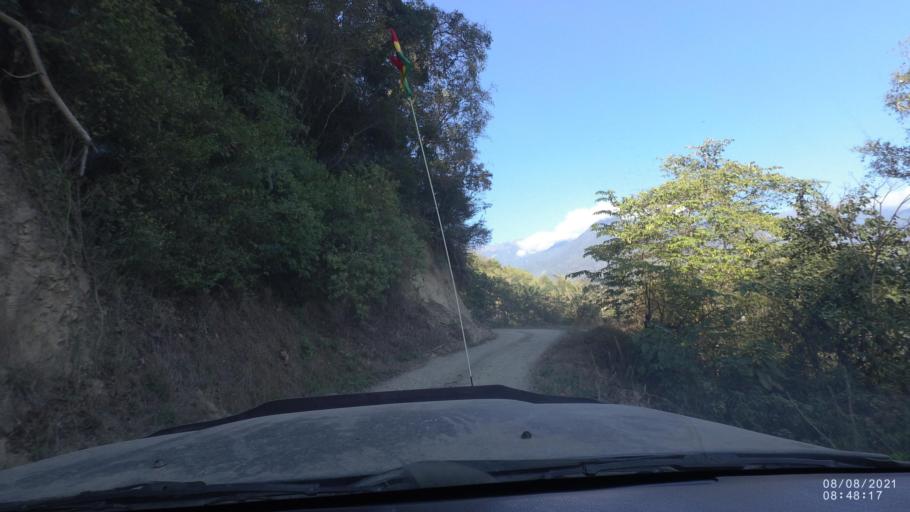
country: BO
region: La Paz
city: Quime
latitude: -16.5303
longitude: -66.7544
